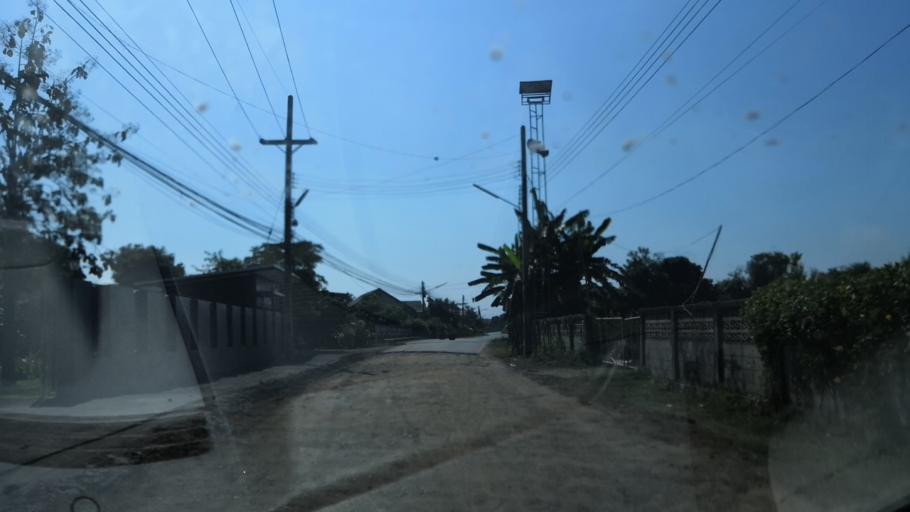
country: TH
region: Chiang Rai
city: Wiang Chai
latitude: 19.8898
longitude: 99.9503
